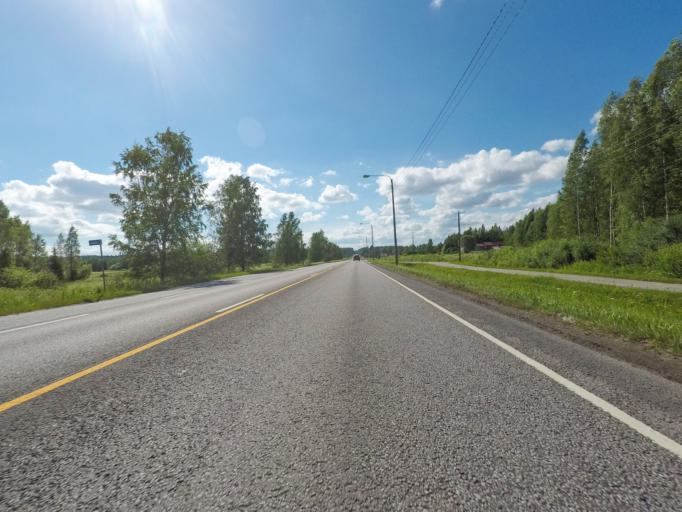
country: FI
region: Southern Savonia
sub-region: Savonlinna
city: Savonlinna
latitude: 61.8772
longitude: 28.9922
